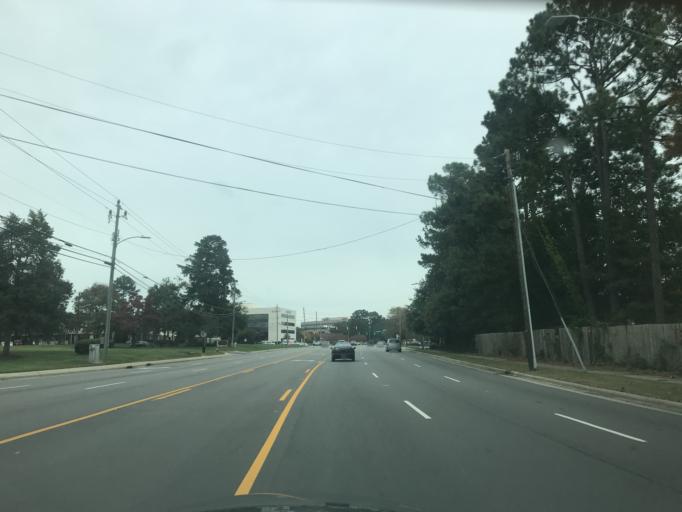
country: US
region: North Carolina
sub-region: Wake County
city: West Raleigh
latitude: 35.8528
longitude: -78.6146
